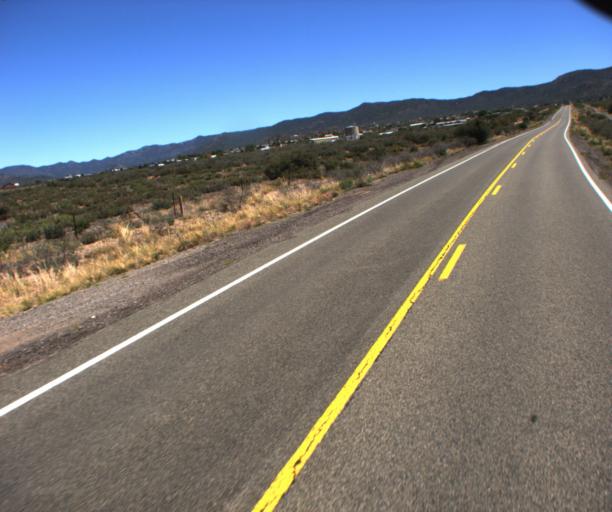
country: US
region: Arizona
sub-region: Yavapai County
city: Prescott
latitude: 34.4097
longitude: -112.6127
